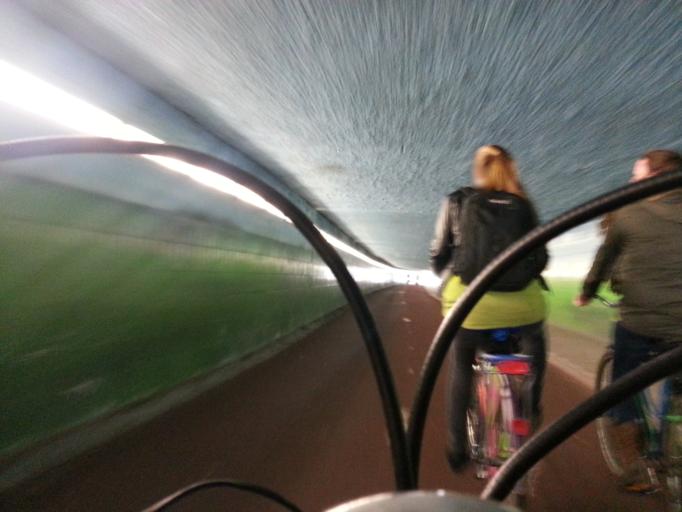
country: NL
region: North Brabant
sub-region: Gemeente Eindhoven
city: Eindhoven
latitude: 51.4429
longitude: 5.4844
